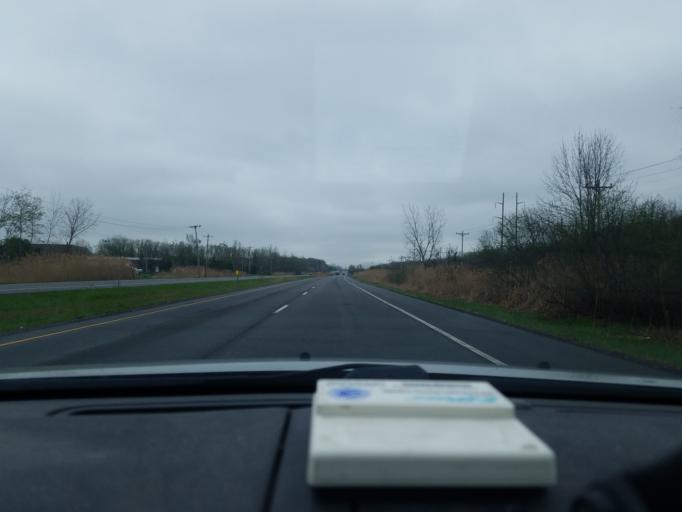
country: US
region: New York
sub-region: Onondaga County
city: East Syracuse
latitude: 43.1189
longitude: -76.0784
